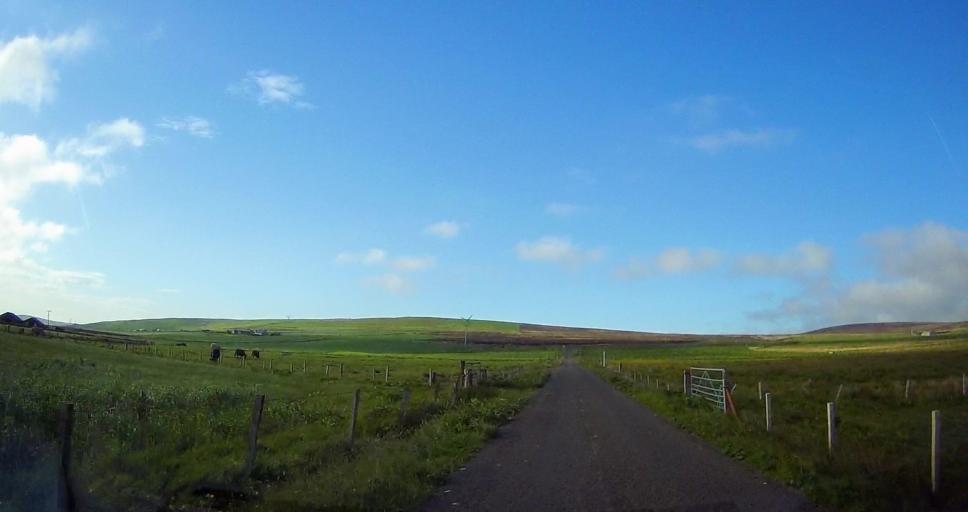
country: GB
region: Scotland
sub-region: Orkney Islands
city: Stromness
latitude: 59.0884
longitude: -3.1828
